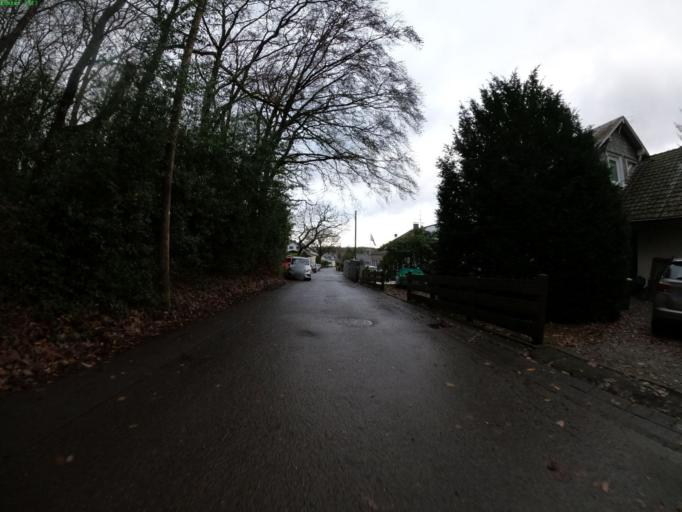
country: DE
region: North Rhine-Westphalia
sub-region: Regierungsbezirk Dusseldorf
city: Remscheid
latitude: 51.1830
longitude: 7.1396
